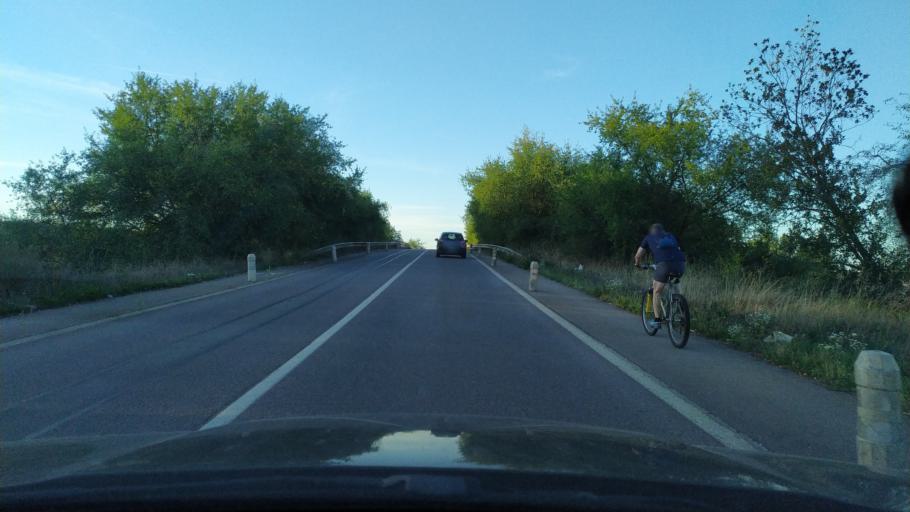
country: FR
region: Lorraine
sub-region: Departement de la Moselle
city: Maizieres-les-Metz
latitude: 49.2056
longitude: 6.1489
